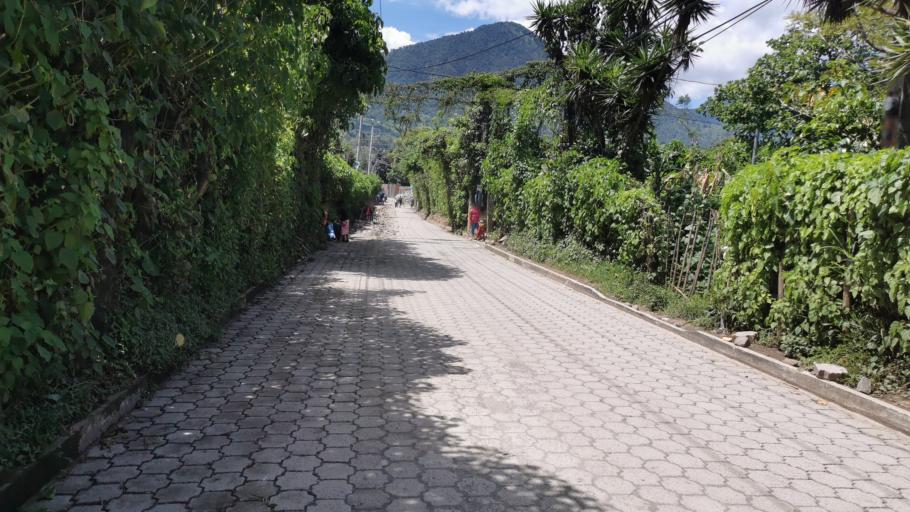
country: GT
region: Guatemala
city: Amatitlan
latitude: 14.4843
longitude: -90.6376
